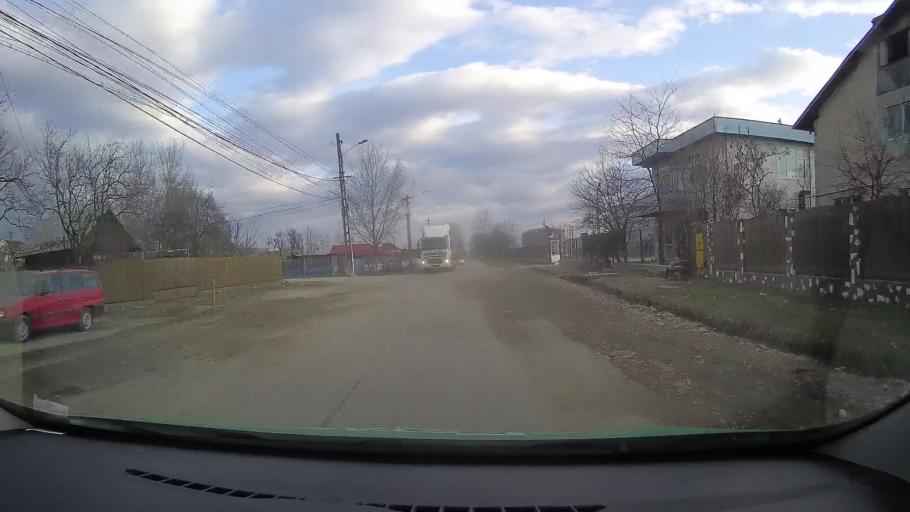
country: RO
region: Dambovita
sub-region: Municipiul Moreni
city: Moreni
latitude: 44.9667
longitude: 25.6538
